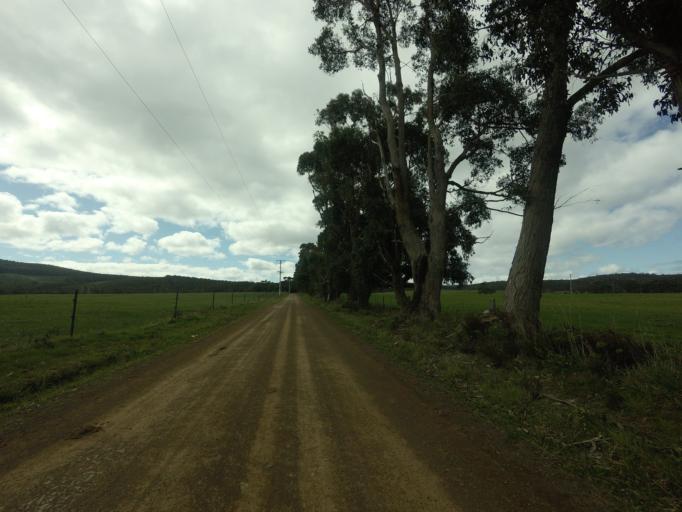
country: AU
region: Tasmania
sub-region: Huon Valley
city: Geeveston
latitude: -43.4321
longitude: 146.9894
